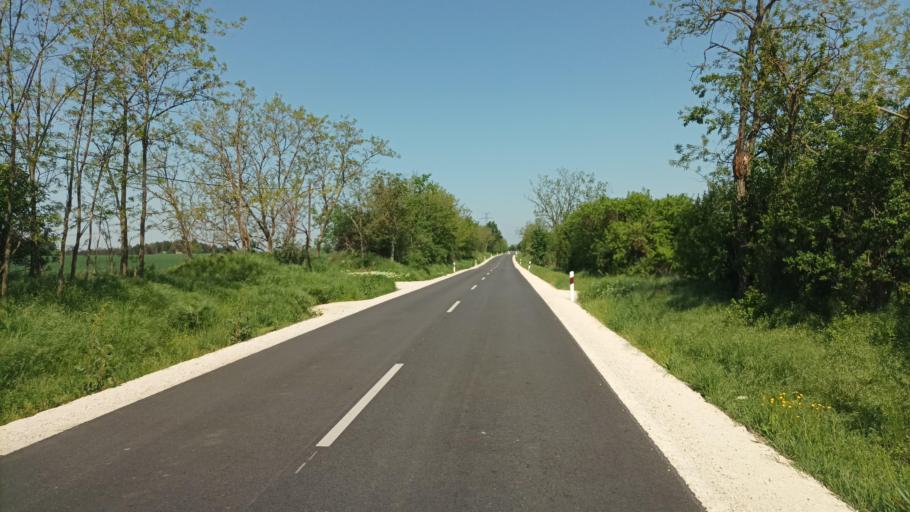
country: HU
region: Pest
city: Gomba
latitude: 47.3798
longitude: 19.5128
